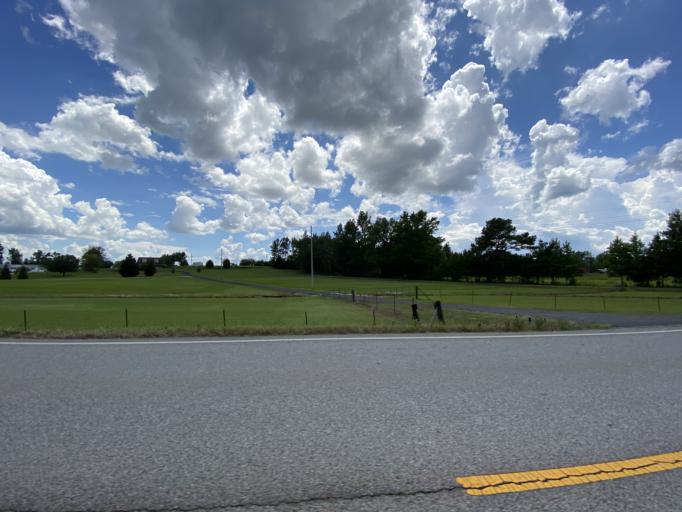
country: US
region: Alabama
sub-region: Lauderdale County
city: Underwood-Petersville
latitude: 34.9468
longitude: -87.8653
